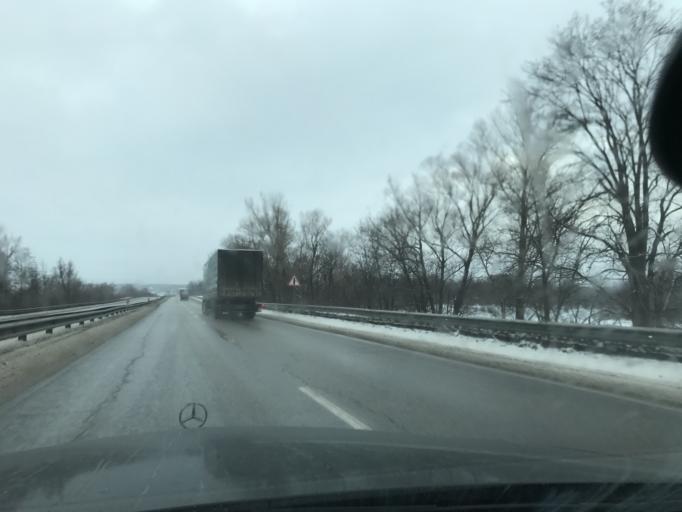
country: RU
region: Vladimir
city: Gorokhovets
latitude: 56.2070
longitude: 42.7307
